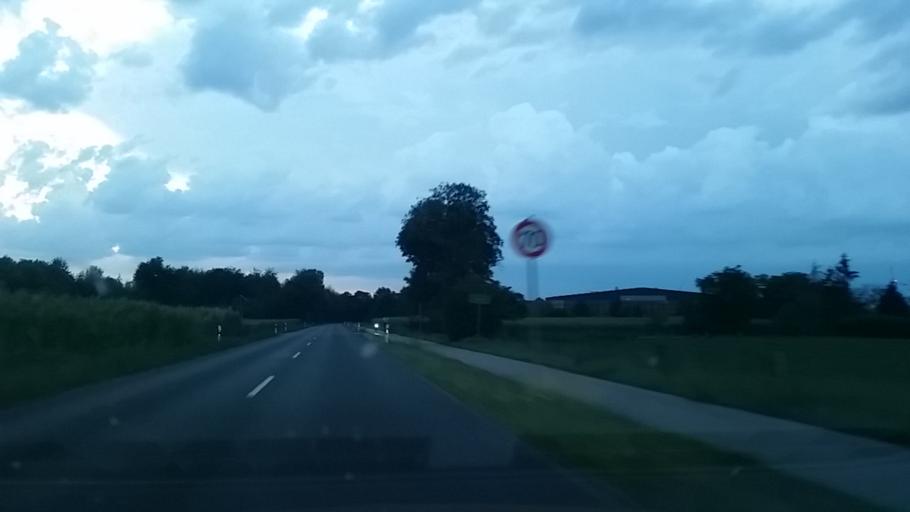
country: DE
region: North Rhine-Westphalia
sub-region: Regierungsbezirk Dusseldorf
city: Kaarst
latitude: 51.2506
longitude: 6.6064
